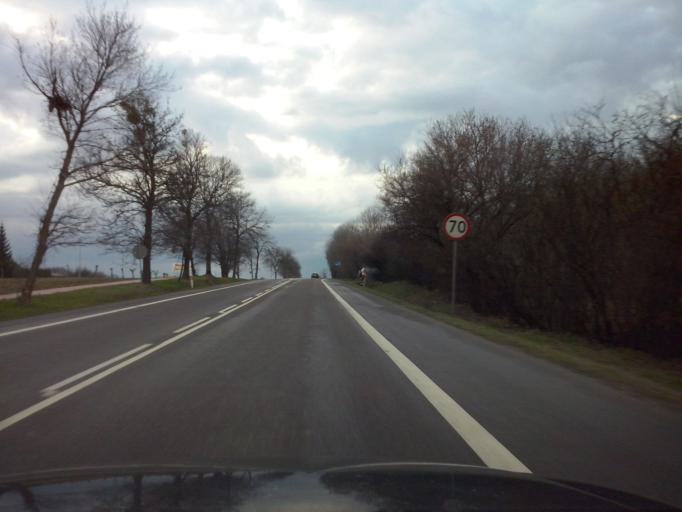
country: PL
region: Lublin Voivodeship
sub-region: Chelm
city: Chelm
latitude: 51.1580
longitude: 23.4020
